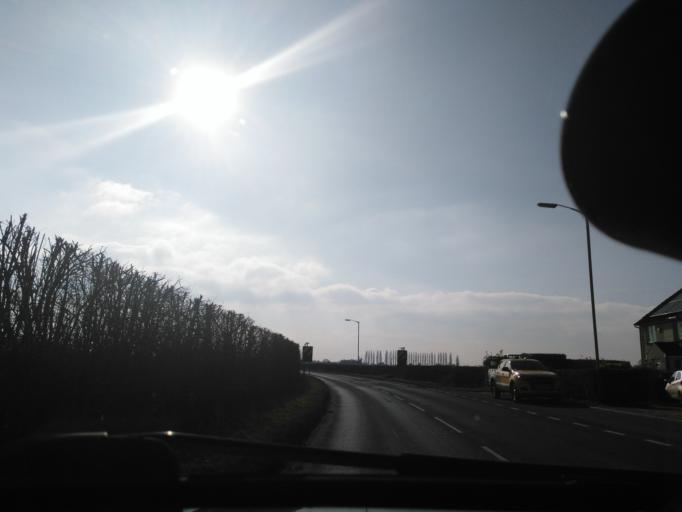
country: GB
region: England
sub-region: Wiltshire
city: Malmesbury
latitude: 51.5510
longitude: -2.1142
